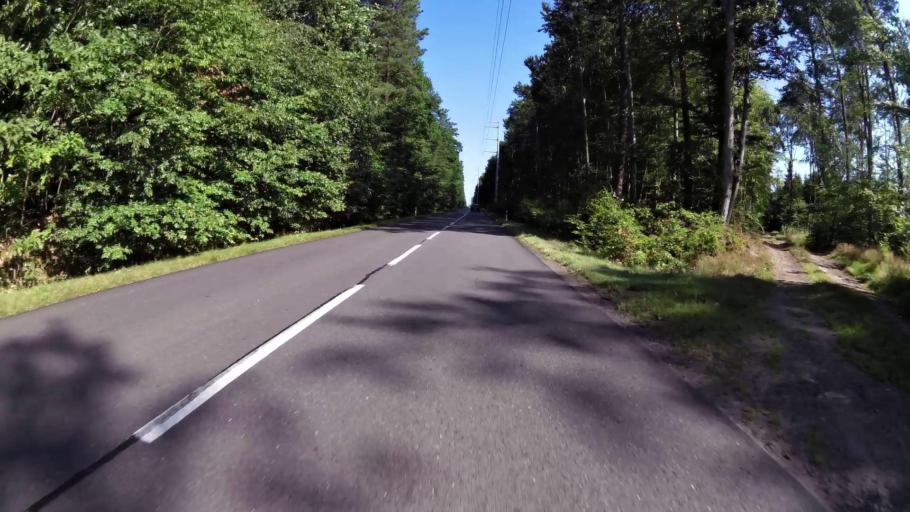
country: PL
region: West Pomeranian Voivodeship
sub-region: Powiat drawski
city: Czaplinek
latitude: 53.4492
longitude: 16.2131
